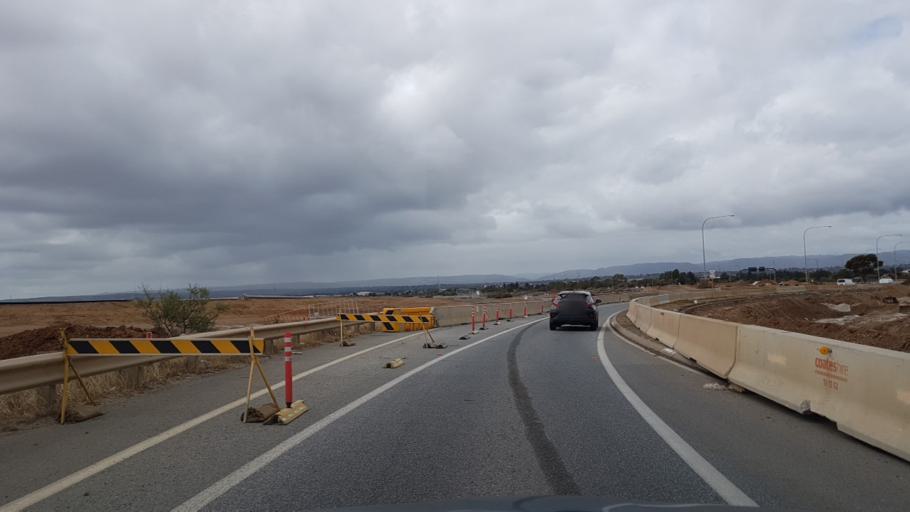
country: AU
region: South Australia
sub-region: Port Adelaide Enfield
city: Blair Athol
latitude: -34.8306
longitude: 138.5655
